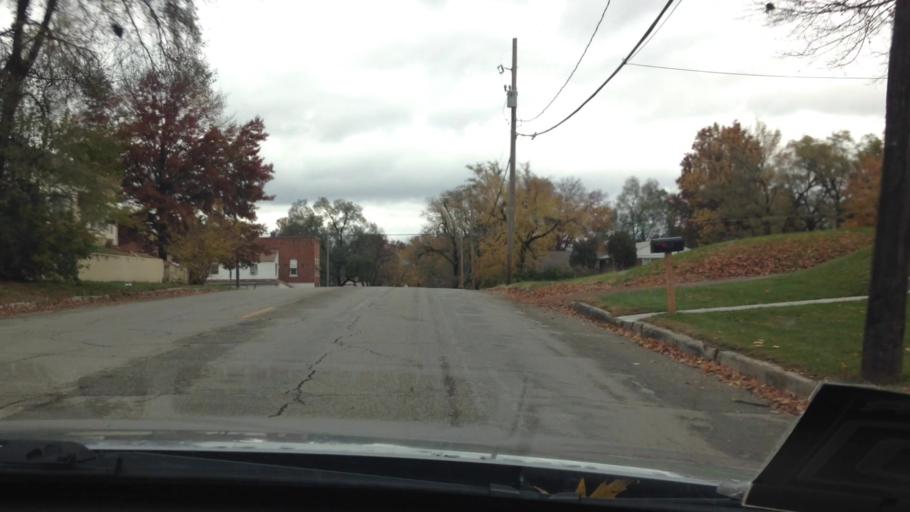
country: US
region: Kansas
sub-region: Leavenworth County
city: Leavenworth
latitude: 39.3023
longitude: -94.9175
